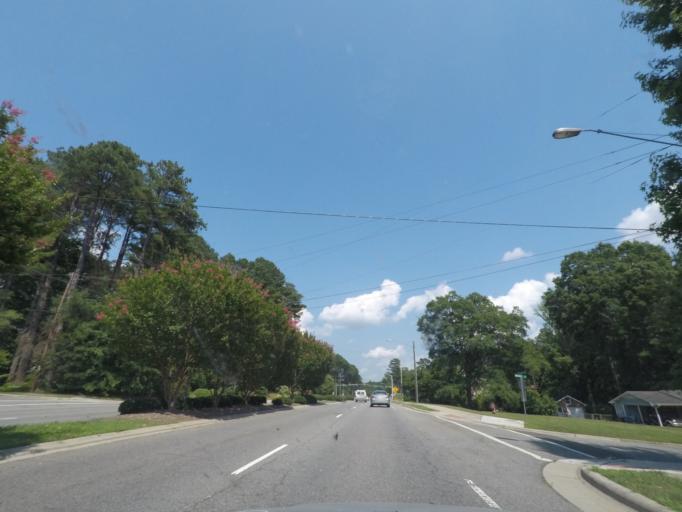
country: US
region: North Carolina
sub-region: Durham County
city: Durham
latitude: 35.9585
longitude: -78.9419
